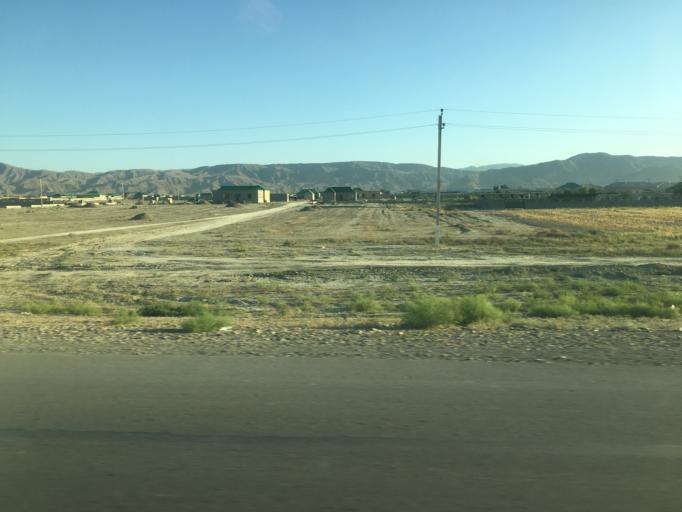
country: TM
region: Ahal
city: Baharly
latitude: 38.3122
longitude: 57.6108
